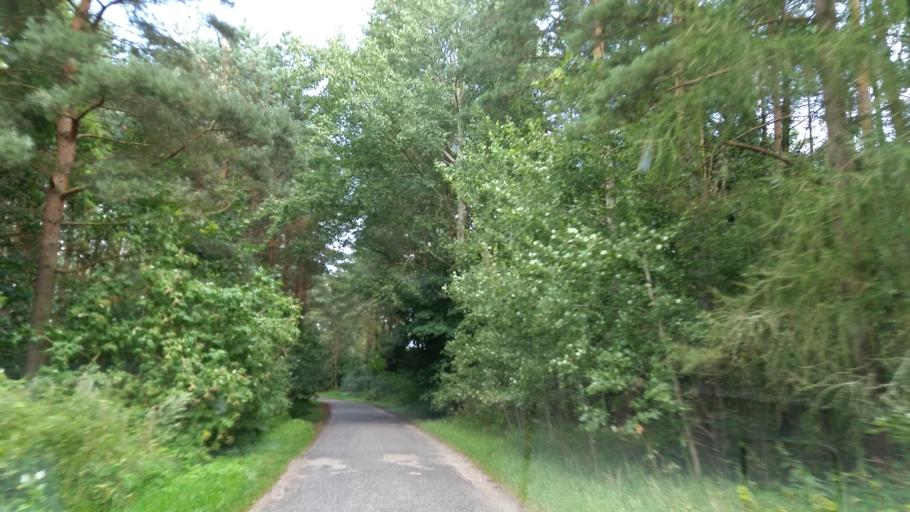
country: PL
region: West Pomeranian Voivodeship
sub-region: Powiat choszczenski
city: Krzecin
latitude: 53.0868
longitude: 15.4860
